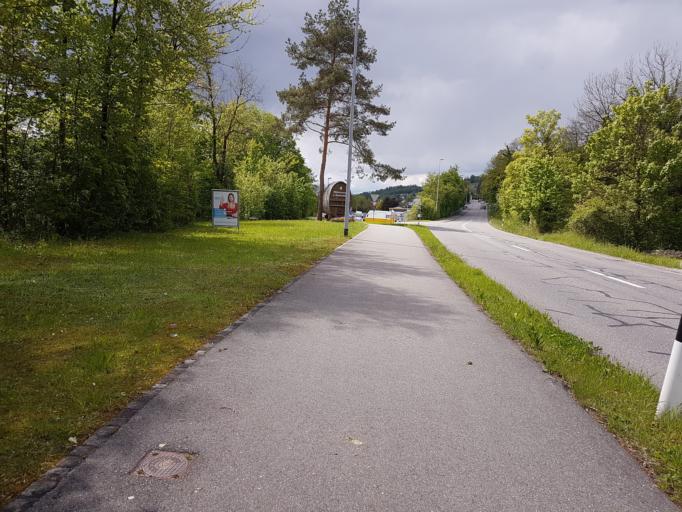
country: CH
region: Aargau
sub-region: Bezirk Brugg
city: Veltheim
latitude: 47.4152
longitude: 8.1497
